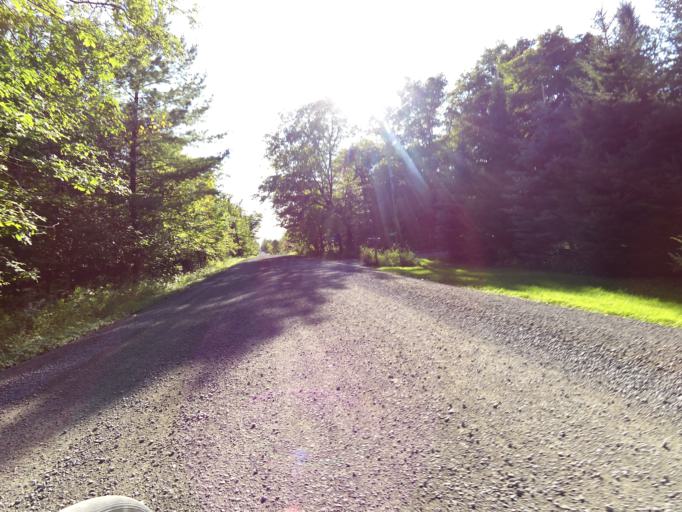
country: CA
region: Ontario
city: Bells Corners
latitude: 45.4860
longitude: -76.0363
